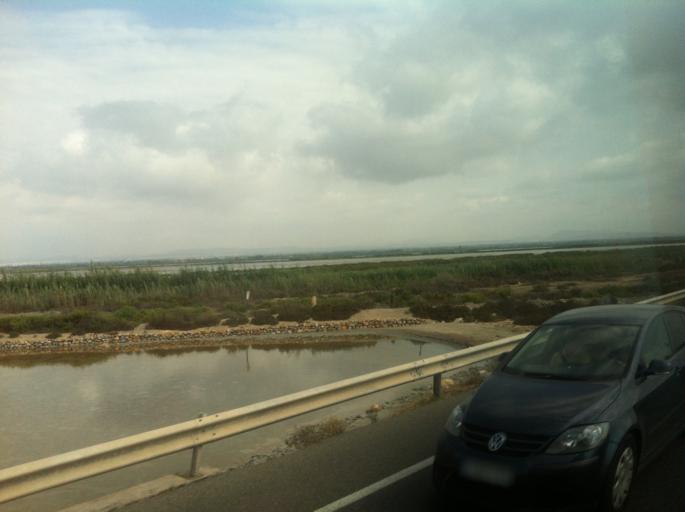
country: ES
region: Valencia
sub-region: Provincia de Alicante
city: Santa Pola
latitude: 38.1778
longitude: -0.6201
